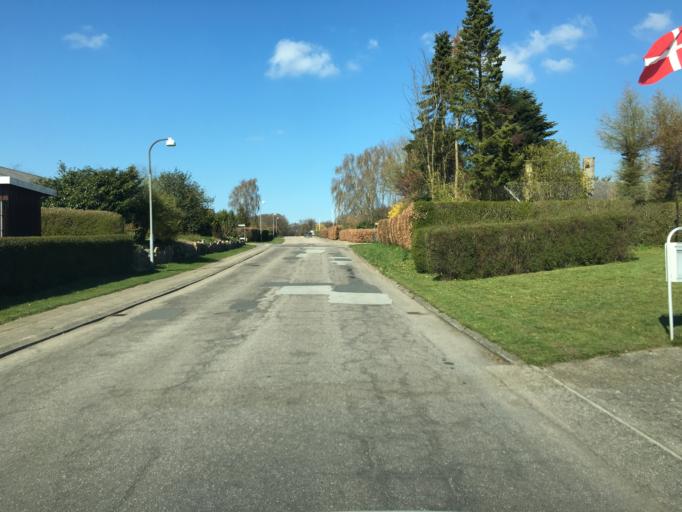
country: DK
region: South Denmark
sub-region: Aabenraa Kommune
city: Krusa
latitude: 54.9296
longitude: 9.4448
